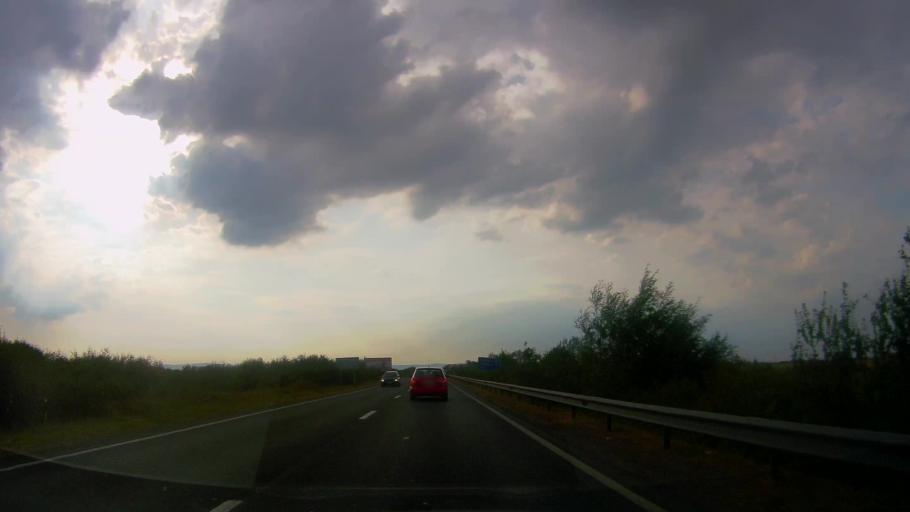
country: RO
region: Satu Mare
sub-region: Oras Ardud
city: Madaras
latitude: 47.7262
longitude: 22.8853
